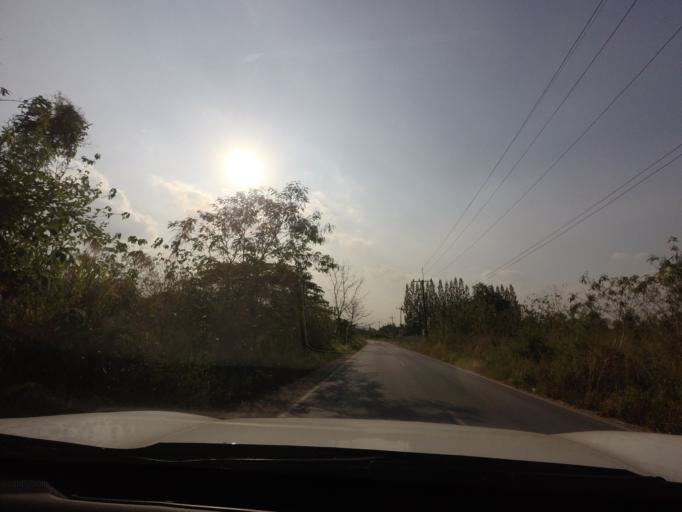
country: TH
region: Nakhon Ratchasima
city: Pak Chong
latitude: 14.6231
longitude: 101.4484
